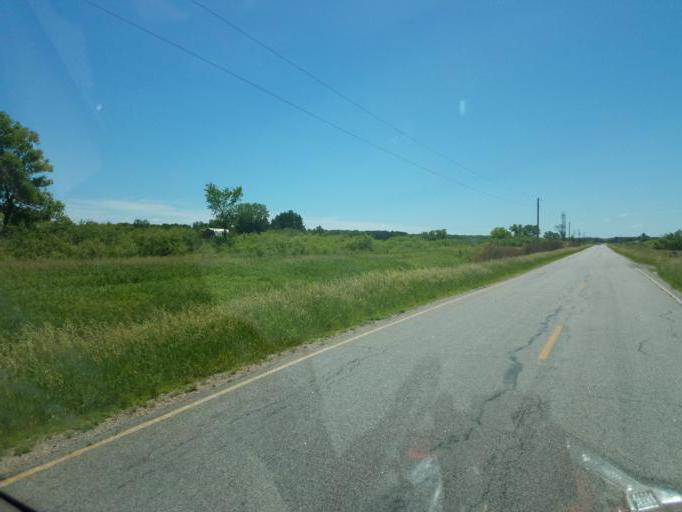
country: US
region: Wisconsin
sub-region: Juneau County
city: New Lisbon
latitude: 44.0136
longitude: -90.2717
